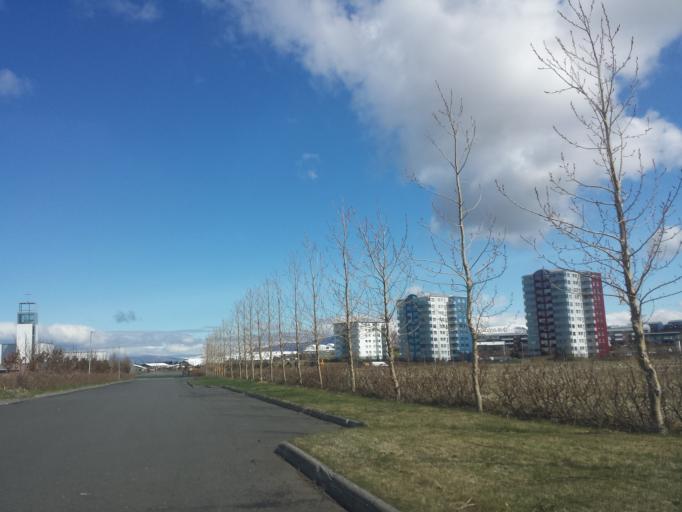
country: IS
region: Capital Region
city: Kopavogur
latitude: 64.0924
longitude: -21.8631
